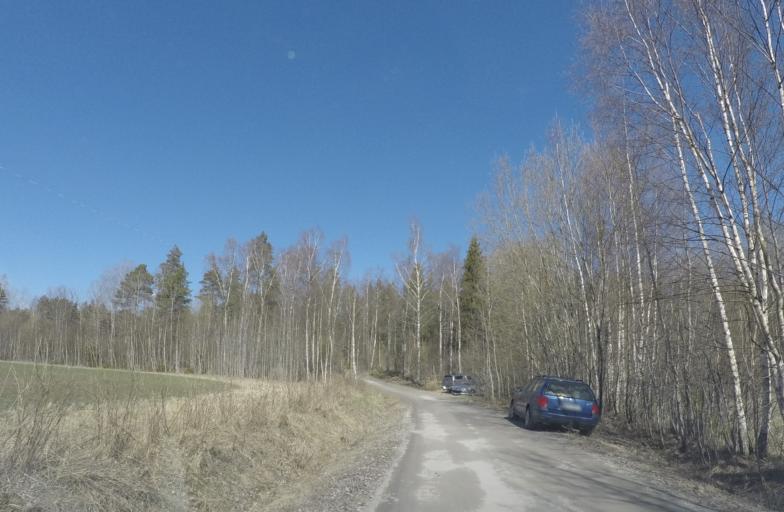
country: SE
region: Vaestmanland
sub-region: Vasteras
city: Vasteras
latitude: 59.6645
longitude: 16.4968
